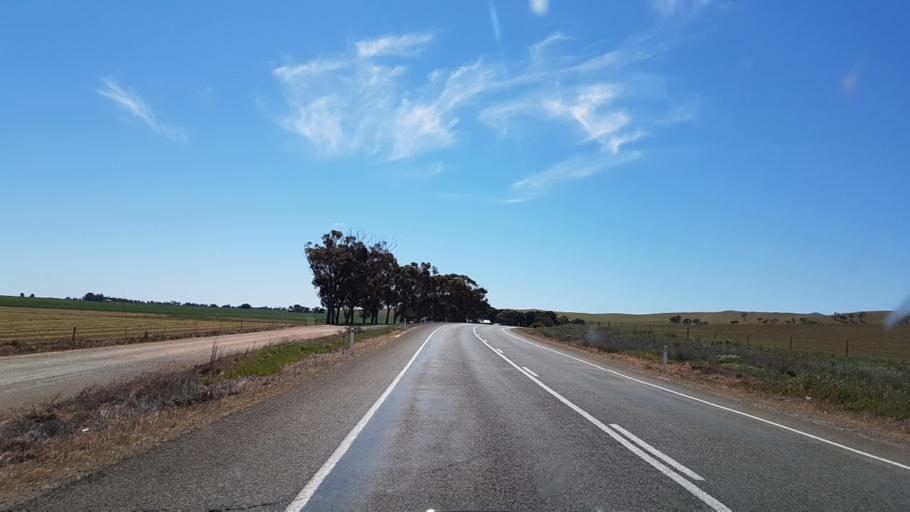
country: AU
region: South Australia
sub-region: Northern Areas
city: Jamestown
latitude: -33.4520
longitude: 138.8941
